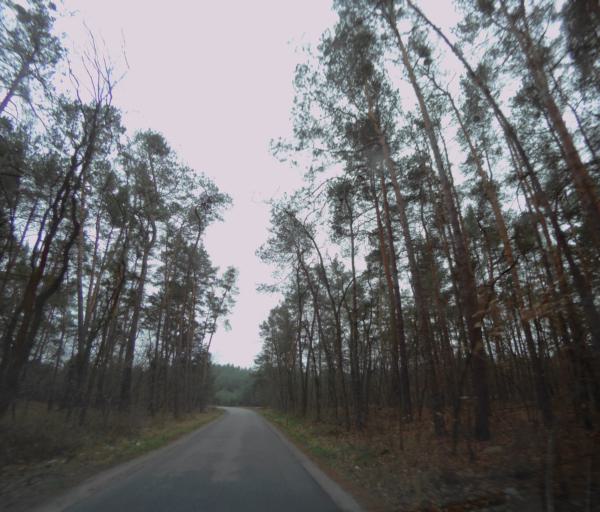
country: PL
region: Subcarpathian Voivodeship
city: Nowa Sarzyna
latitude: 50.3012
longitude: 22.3475
